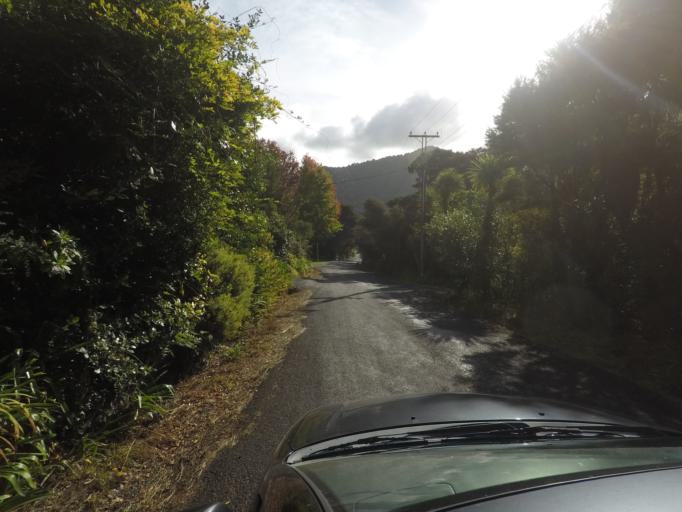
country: NZ
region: Auckland
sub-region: Auckland
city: Titirangi
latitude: -36.9975
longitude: 174.5751
